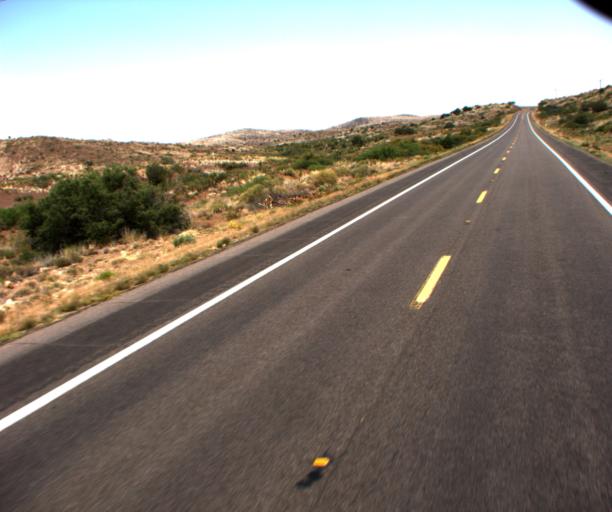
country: US
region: Arizona
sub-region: Greenlee County
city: Clifton
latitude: 32.7713
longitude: -109.2688
